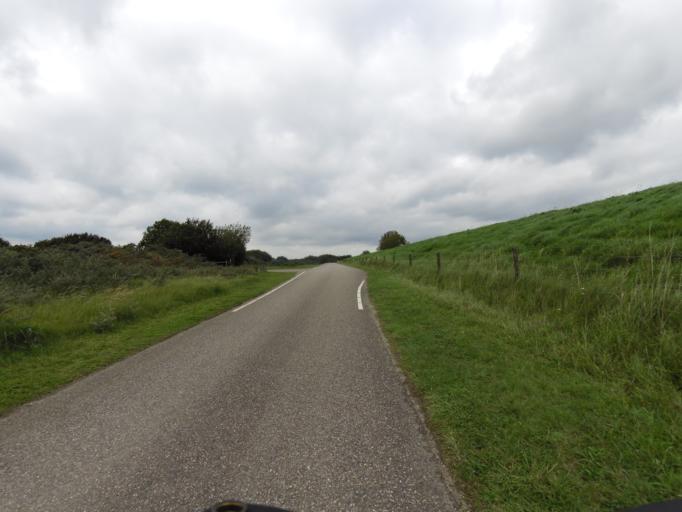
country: NL
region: South Holland
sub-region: Gemeente Goeree-Overflakkee
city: Dirksland
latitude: 51.7697
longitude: 4.0353
